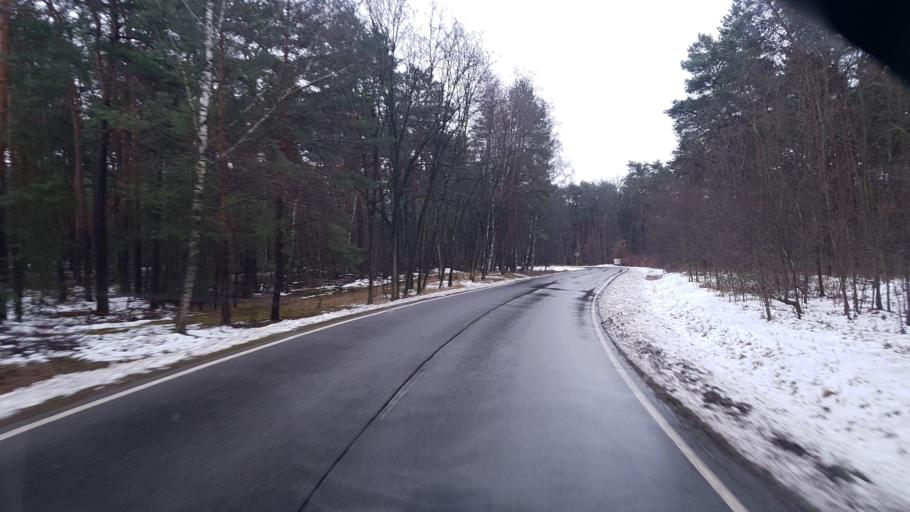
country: DE
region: Brandenburg
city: Schenkendobern
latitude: 51.9069
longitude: 14.6290
